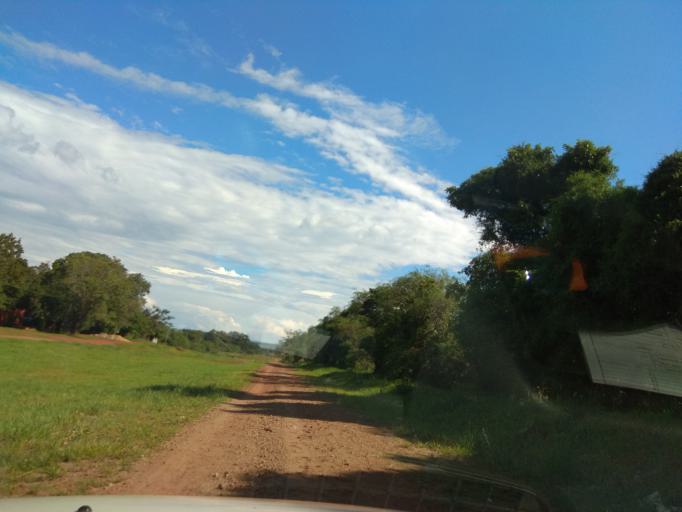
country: AR
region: Misiones
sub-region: Departamento de Candelaria
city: Candelaria
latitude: -27.4624
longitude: -55.7555
